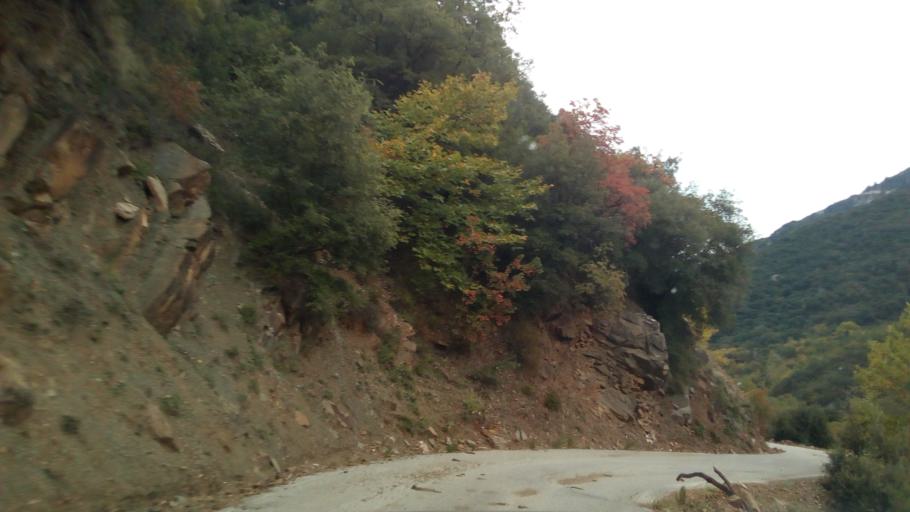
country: GR
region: West Greece
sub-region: Nomos Aitolias kai Akarnanias
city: Thermo
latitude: 38.5965
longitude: 21.8475
